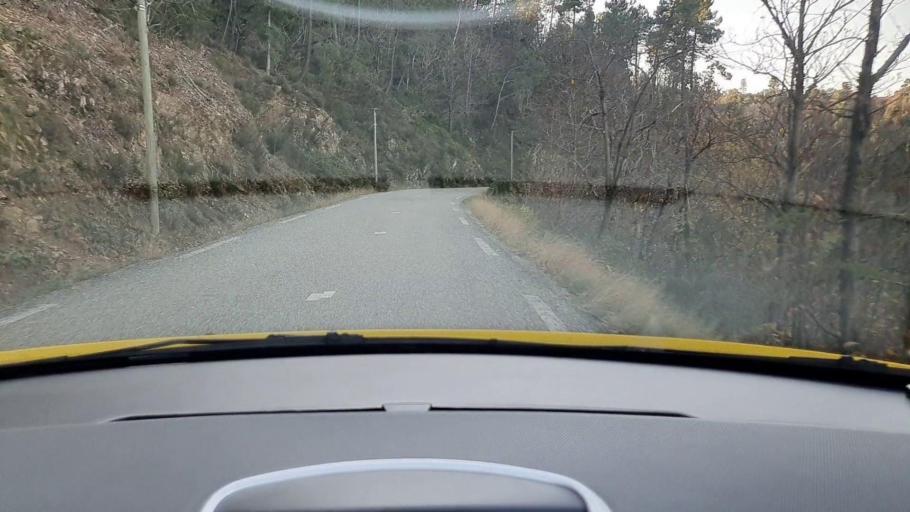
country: FR
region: Languedoc-Roussillon
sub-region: Departement du Gard
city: Branoux-les-Taillades
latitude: 44.2835
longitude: 3.9869
